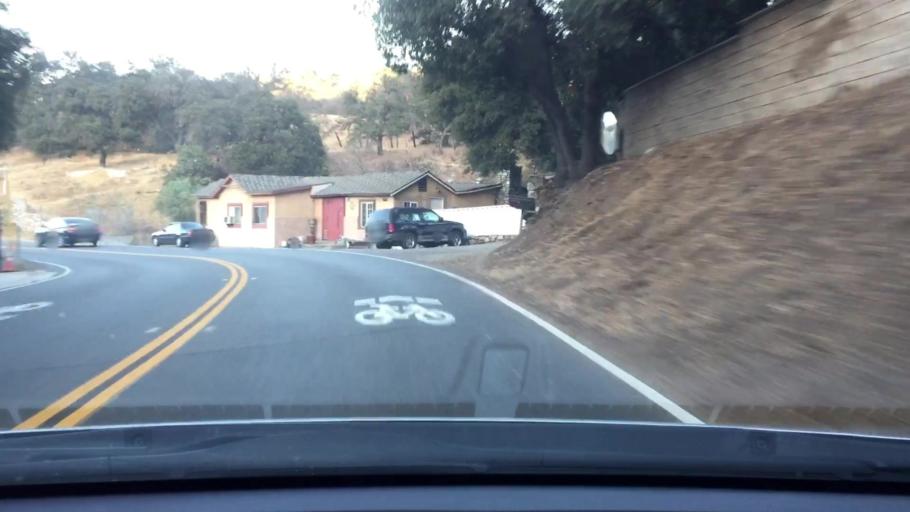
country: US
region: California
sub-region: San Bernardino County
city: Chino Hills
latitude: 33.9489
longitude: -117.7774
